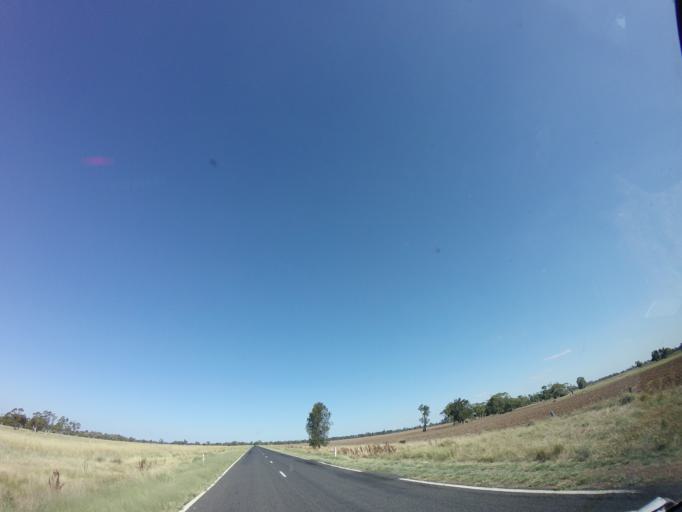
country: AU
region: New South Wales
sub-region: Gilgandra
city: Gilgandra
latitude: -31.6687
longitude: 148.2232
